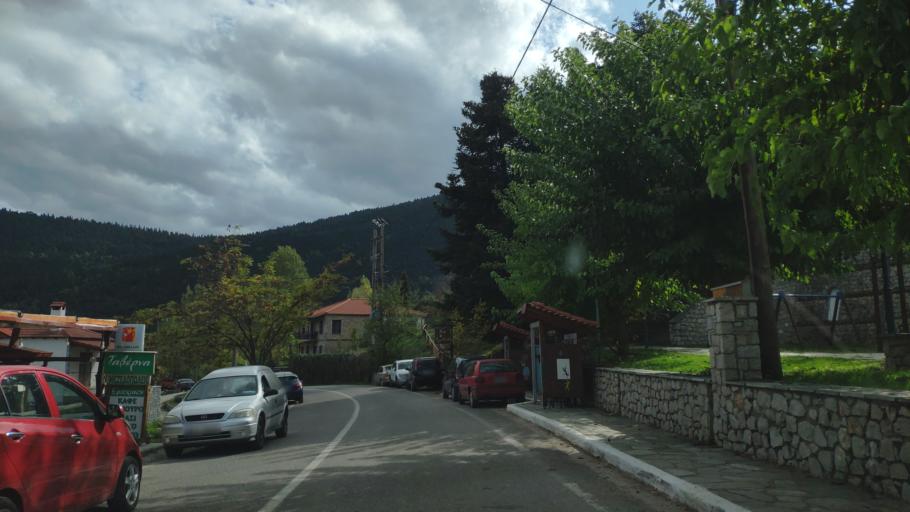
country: GR
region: Central Greece
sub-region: Nomos Fthiotidos
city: Stavros
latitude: 38.7356
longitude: 22.3461
